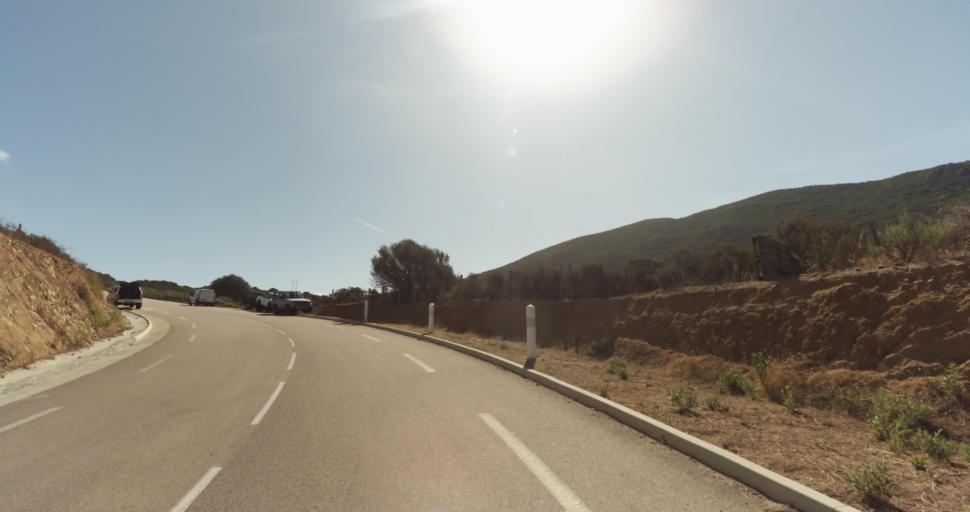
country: FR
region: Corsica
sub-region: Departement de la Corse-du-Sud
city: Ajaccio
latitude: 41.9326
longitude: 8.6722
